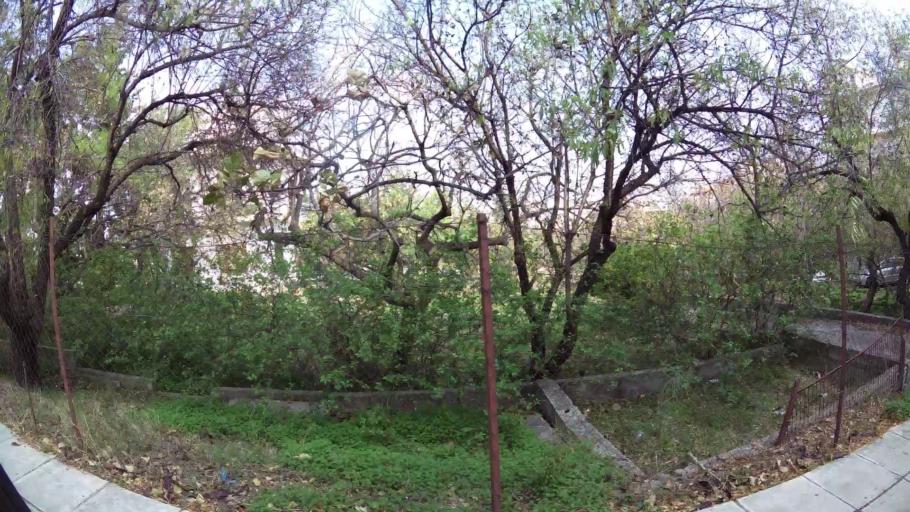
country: GR
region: Attica
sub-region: Nomarchia Athinas
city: Irakleio
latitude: 38.0582
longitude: 23.7650
